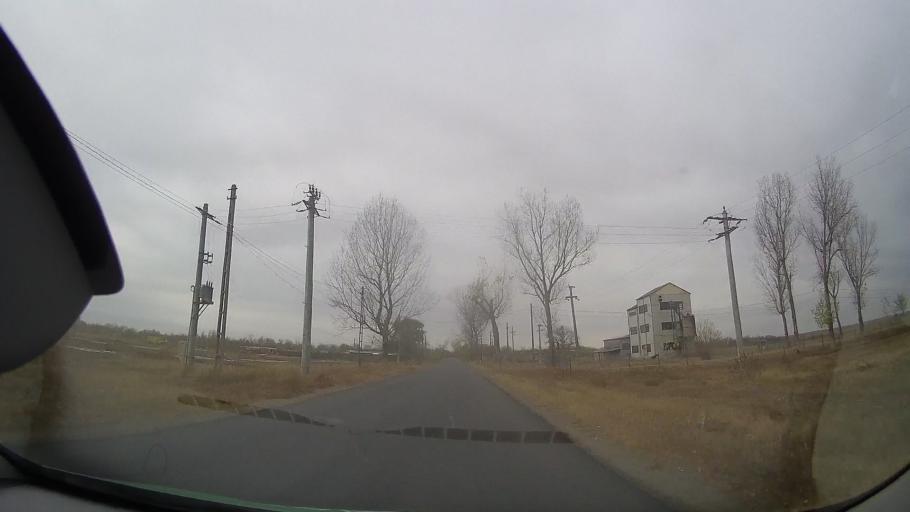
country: RO
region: Braila
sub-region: Comuna Ciresu
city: Ciresu
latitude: 44.9395
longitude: 27.3747
